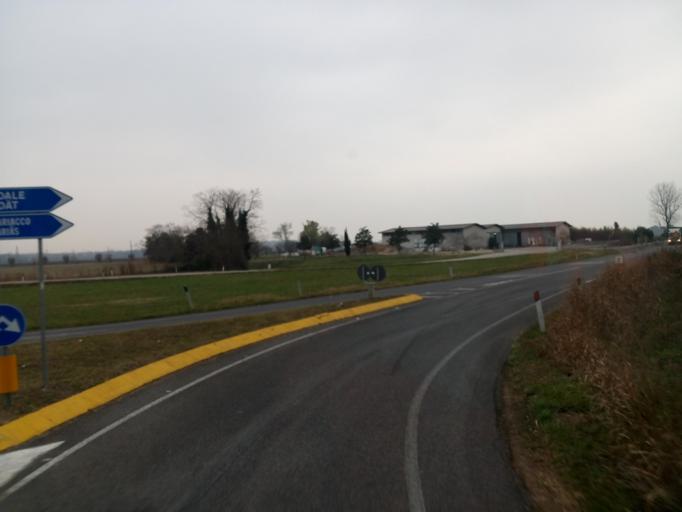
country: IT
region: Friuli Venezia Giulia
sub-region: Provincia di Udine
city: Buttrio
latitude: 46.0282
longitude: 13.3286
